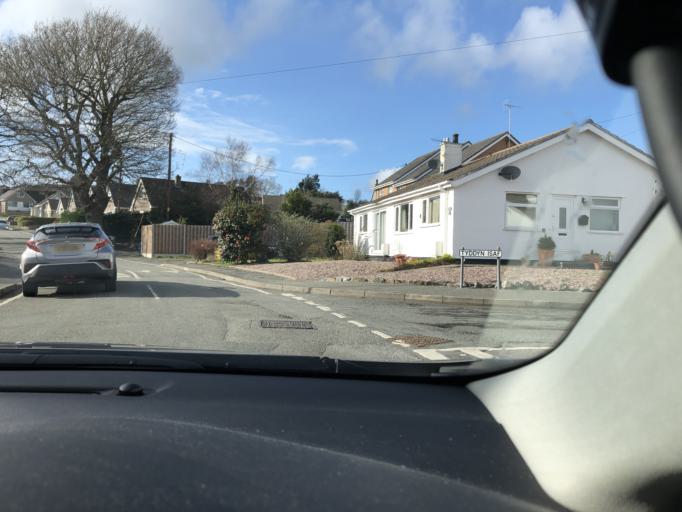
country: GB
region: Wales
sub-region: Anglesey
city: Menai Bridge
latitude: 53.2315
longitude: -4.1712
